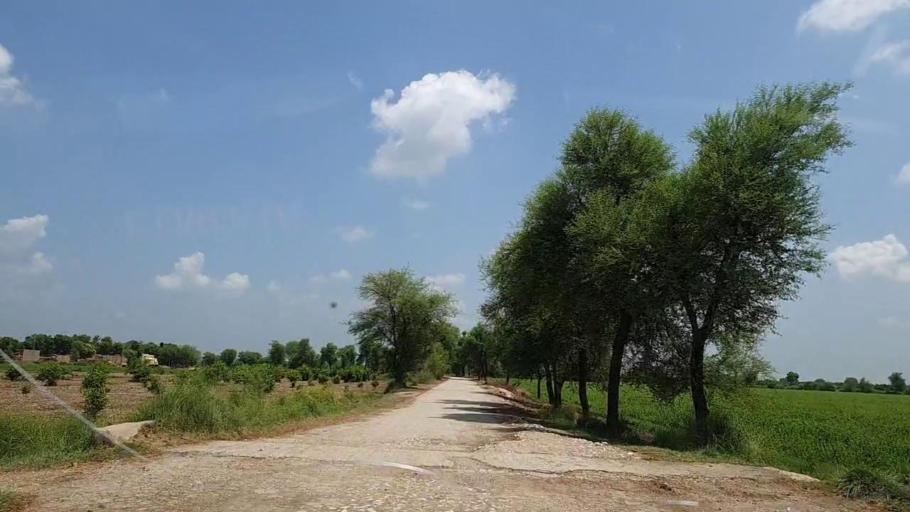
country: PK
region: Sindh
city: Tharu Shah
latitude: 27.0006
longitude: 68.0619
